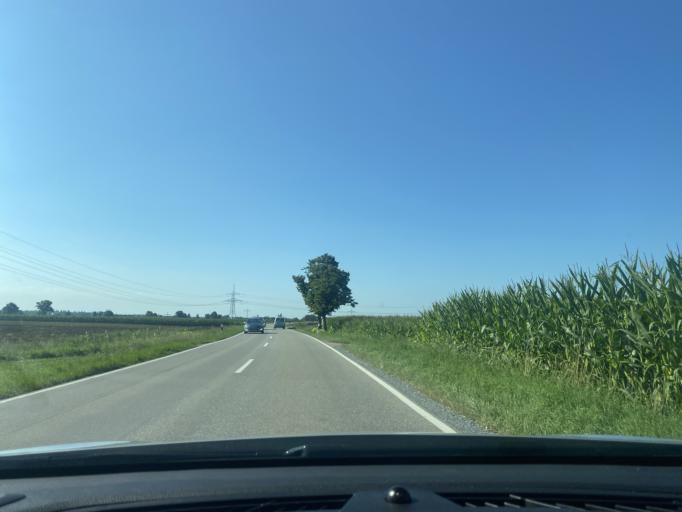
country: DE
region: Bavaria
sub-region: Upper Bavaria
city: Eitting
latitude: 48.3484
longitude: 11.8974
